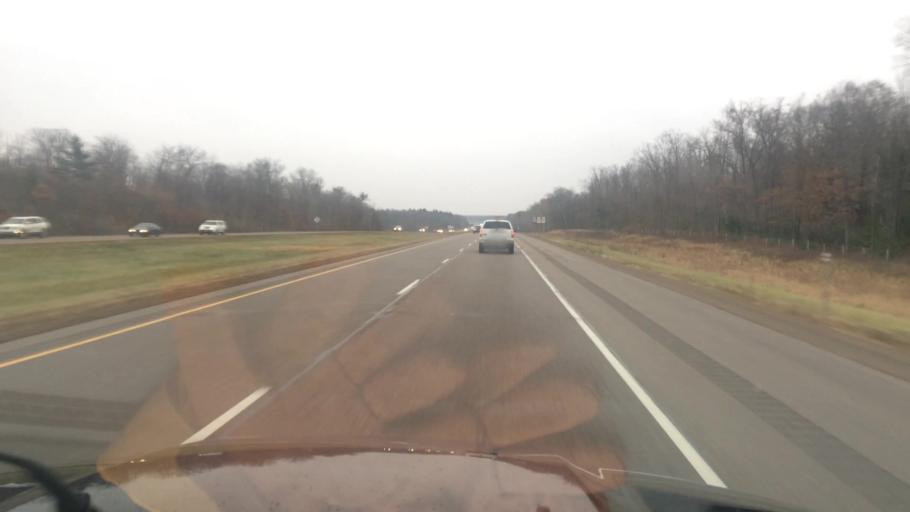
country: US
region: Wisconsin
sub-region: Portage County
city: Stevens Point
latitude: 44.5927
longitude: -89.6126
